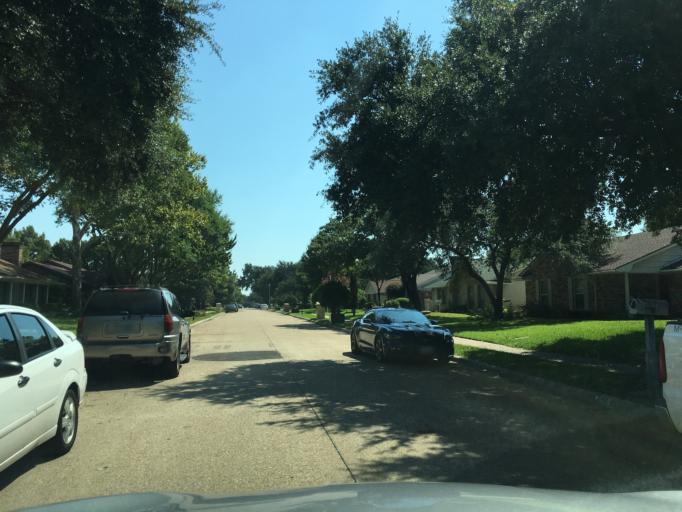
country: US
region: Texas
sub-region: Dallas County
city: Garland
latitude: 32.9358
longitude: -96.6563
